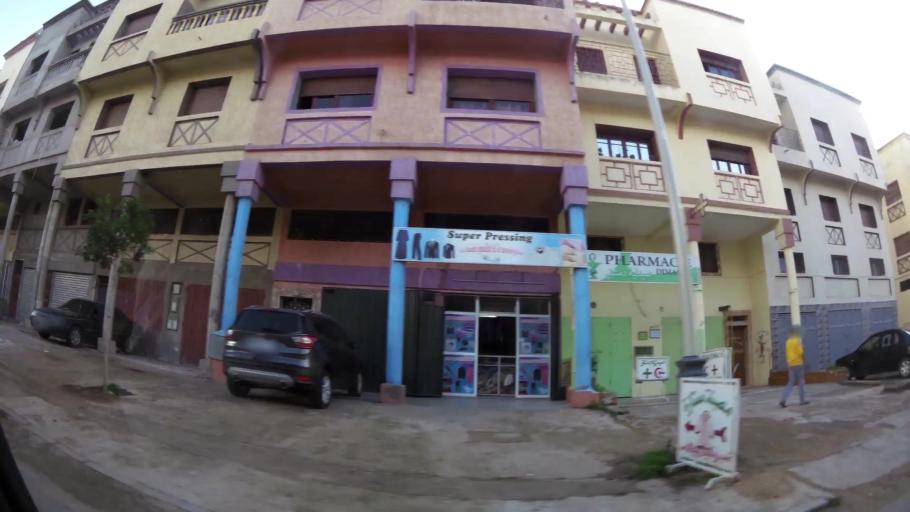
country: MA
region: Chaouia-Ouardigha
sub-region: Settat Province
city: Settat
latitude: 33.0044
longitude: -7.6336
